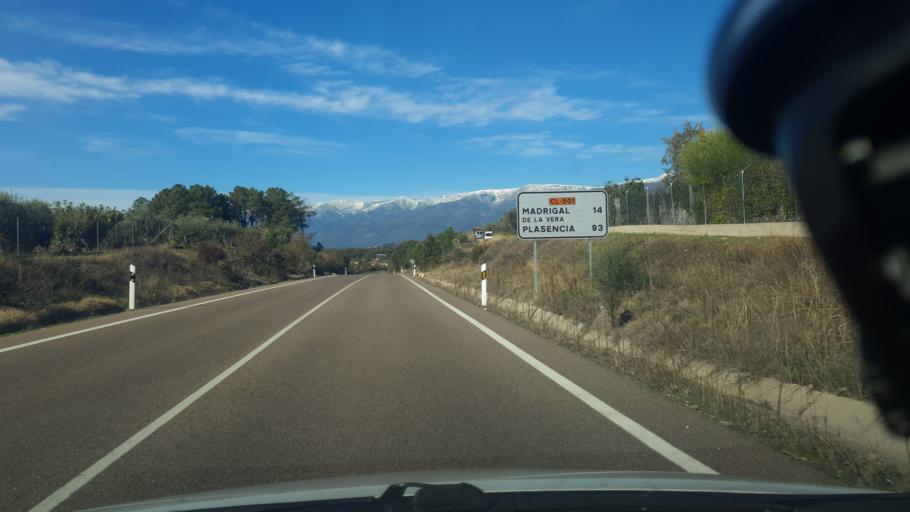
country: ES
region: Castille and Leon
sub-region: Provincia de Avila
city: Candeleda
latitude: 40.1358
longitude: -5.2349
